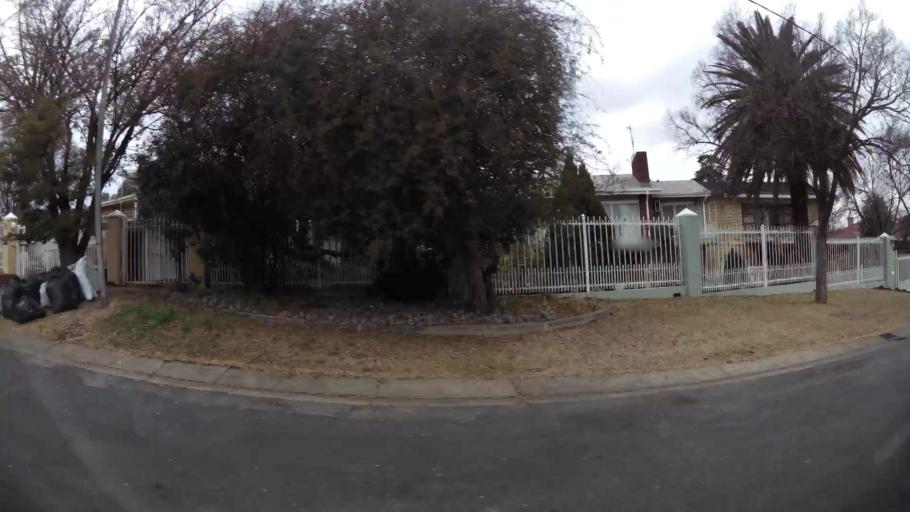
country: ZA
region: Orange Free State
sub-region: Fezile Dabi District Municipality
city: Kroonstad
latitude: -27.6842
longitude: 27.2331
